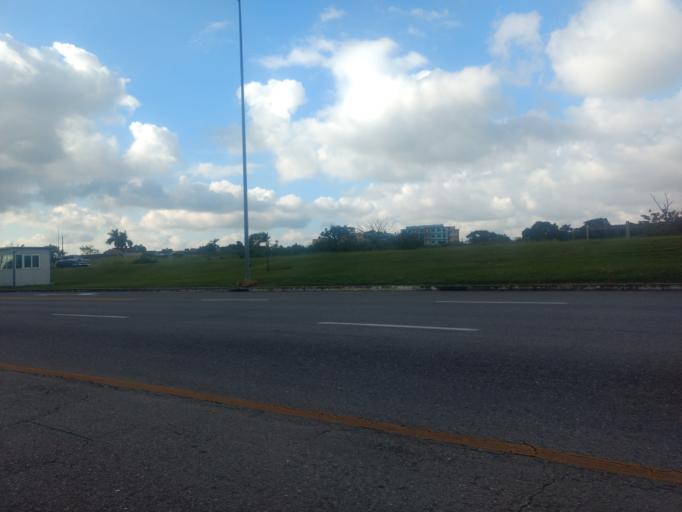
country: CU
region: La Habana
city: Boyeros
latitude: 23.0003
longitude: -82.4083
